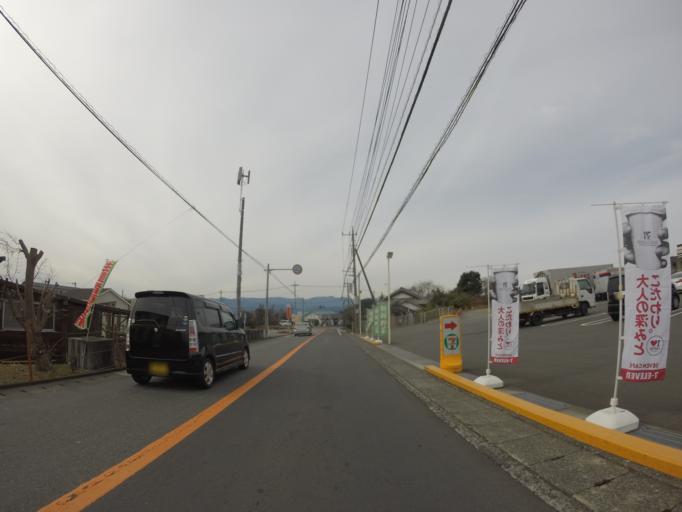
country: JP
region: Shizuoka
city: Fuji
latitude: 35.2113
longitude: 138.6845
